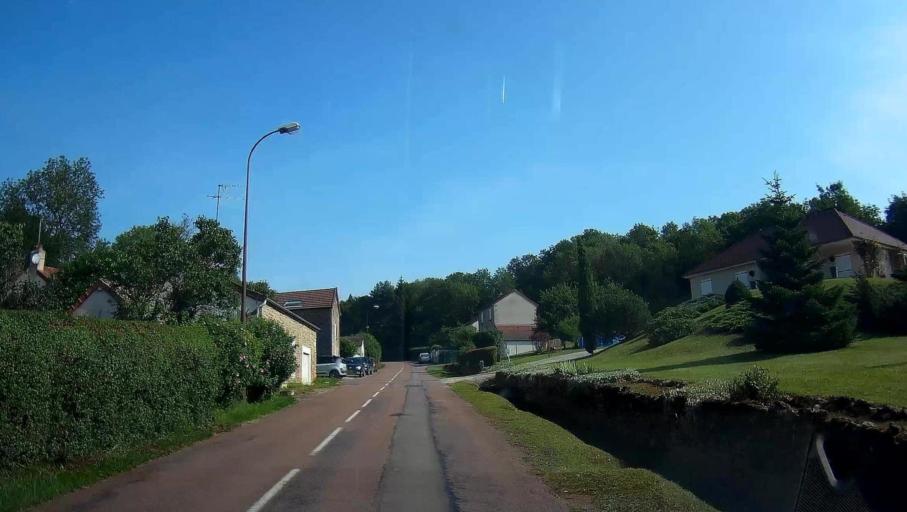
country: FR
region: Bourgogne
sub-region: Departement de Saone-et-Loire
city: Couches
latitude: 46.9003
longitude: 4.5963
